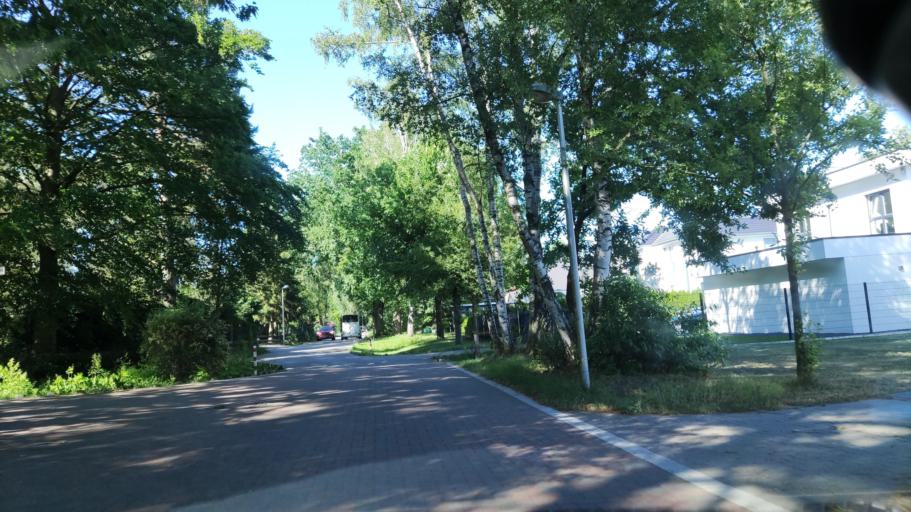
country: DE
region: Lower Saxony
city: Stelle
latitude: 53.3735
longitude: 10.0489
